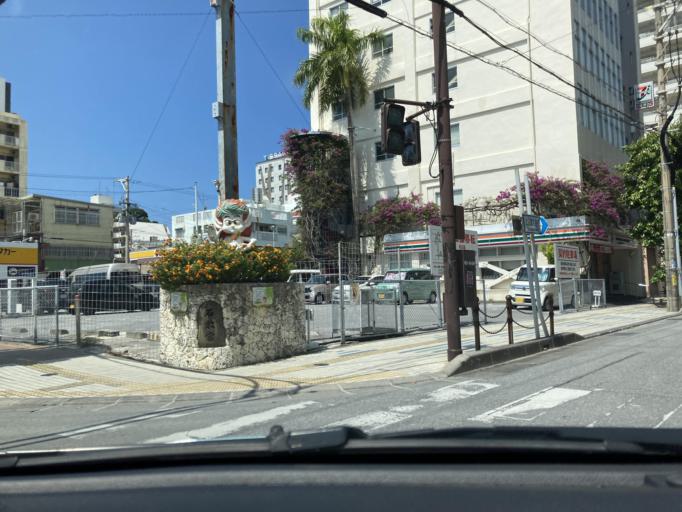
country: JP
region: Okinawa
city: Naha-shi
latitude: 26.2127
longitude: 127.6706
